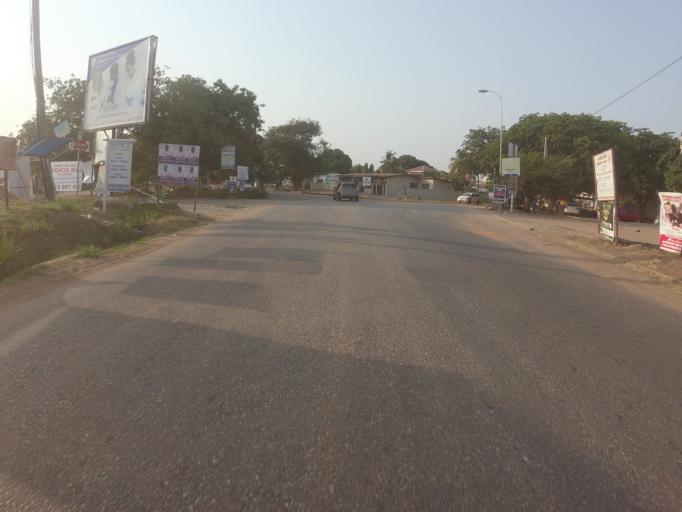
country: GH
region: Greater Accra
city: Nungua
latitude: 5.6221
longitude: -0.0569
